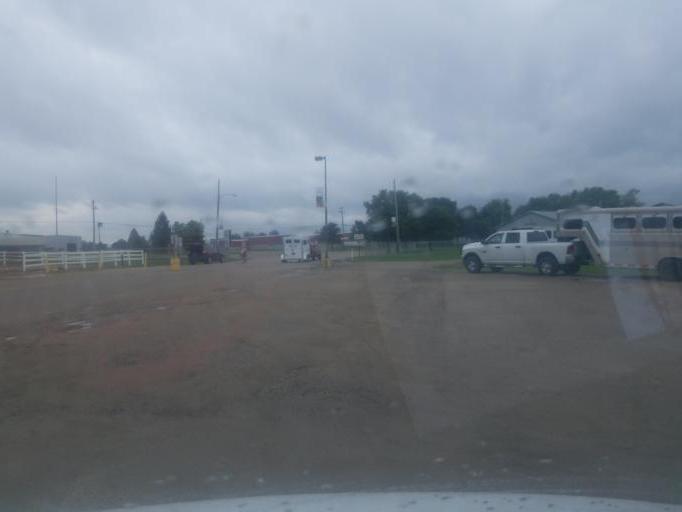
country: US
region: Ohio
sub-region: Clark County
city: Springfield
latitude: 39.8955
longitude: -83.7329
